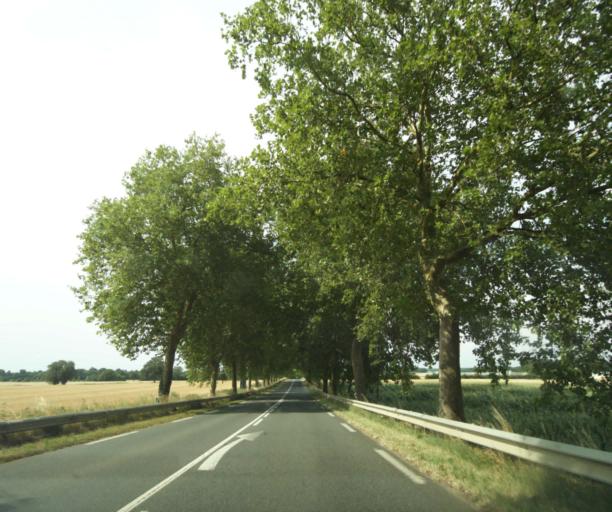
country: FR
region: Centre
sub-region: Departement d'Indre-et-Loire
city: Saint-Christophe-sur-le-Nais
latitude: 47.6219
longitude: 0.5042
